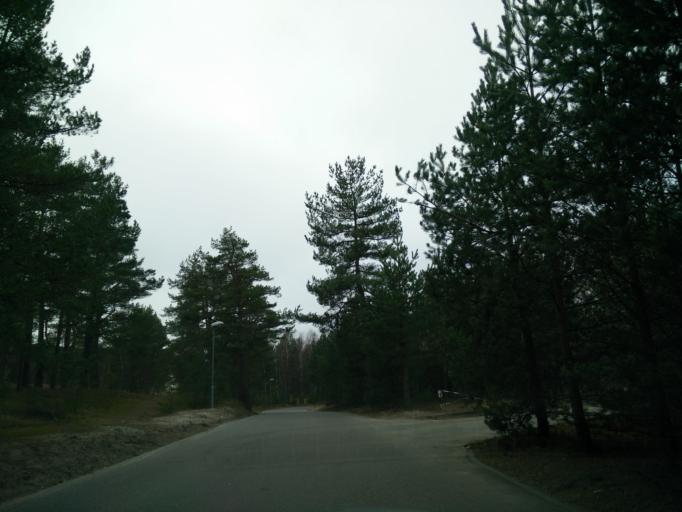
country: LT
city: Nida
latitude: 55.3013
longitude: 20.9908
